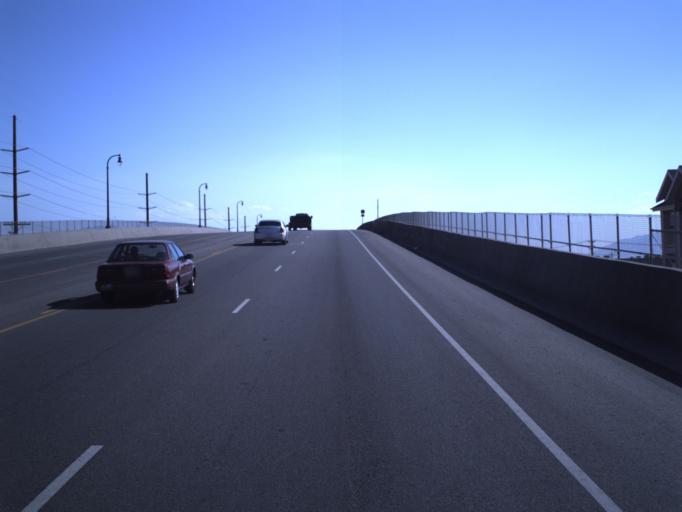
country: US
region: Utah
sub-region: Utah County
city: Orem
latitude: 40.2943
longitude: -111.7342
